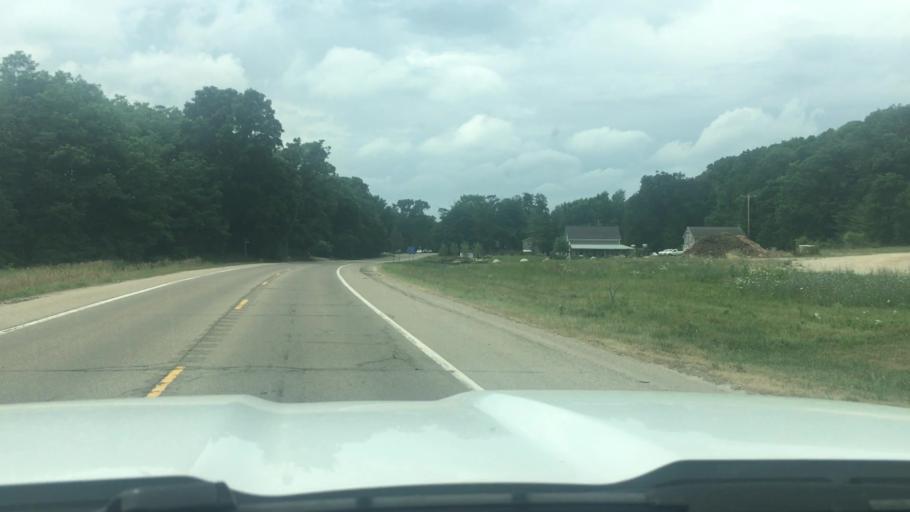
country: US
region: Michigan
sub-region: Kent County
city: Forest Hills
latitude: 42.9286
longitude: -85.4295
